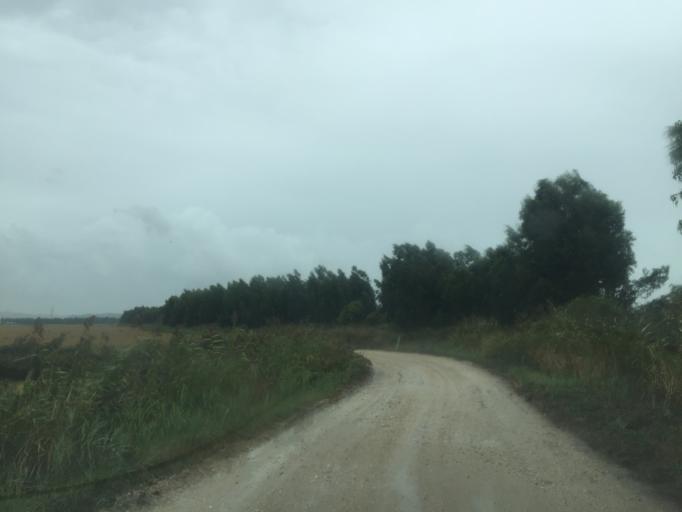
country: PT
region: Coimbra
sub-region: Figueira da Foz
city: Lavos
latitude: 40.1032
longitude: -8.8056
